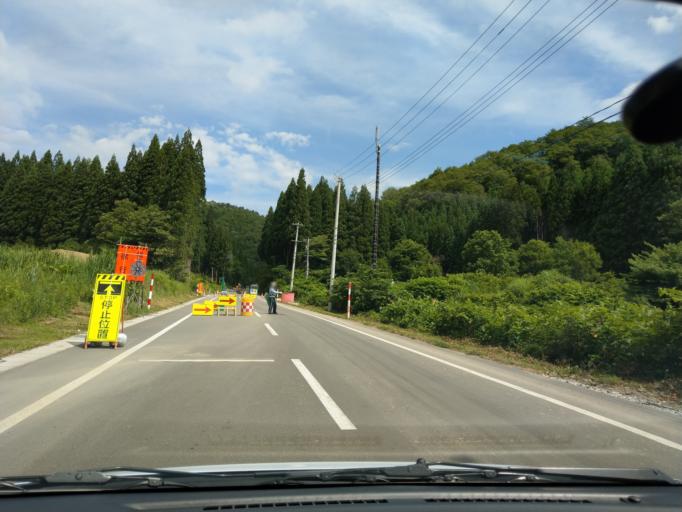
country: JP
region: Akita
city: Kakunodatemachi
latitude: 39.7202
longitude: 140.5847
